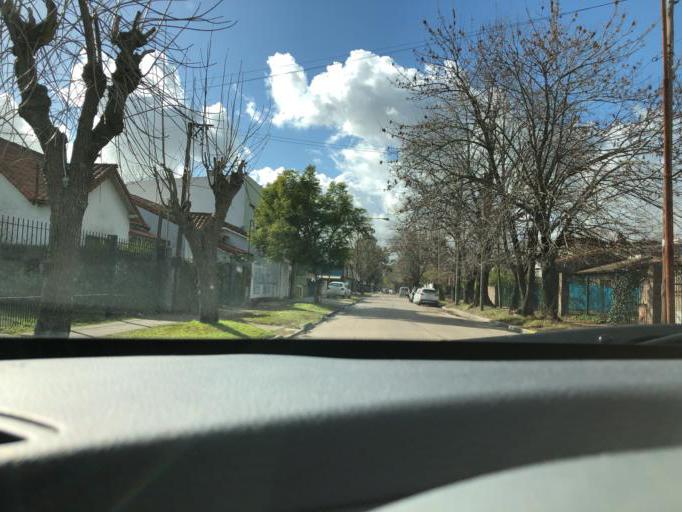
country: AR
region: Buenos Aires
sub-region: Partido de La Plata
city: La Plata
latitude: -34.8719
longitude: -58.0451
